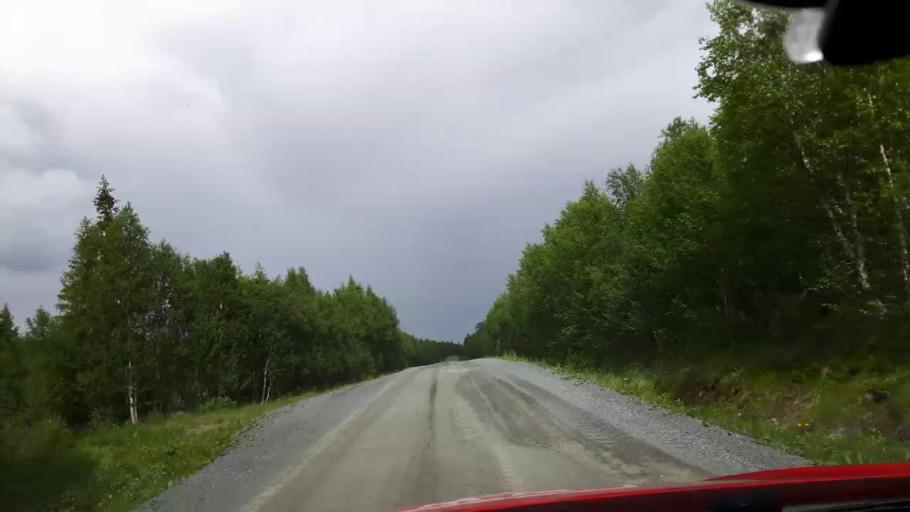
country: NO
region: Nord-Trondelag
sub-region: Lierne
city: Sandvika
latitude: 64.1511
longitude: 13.9790
